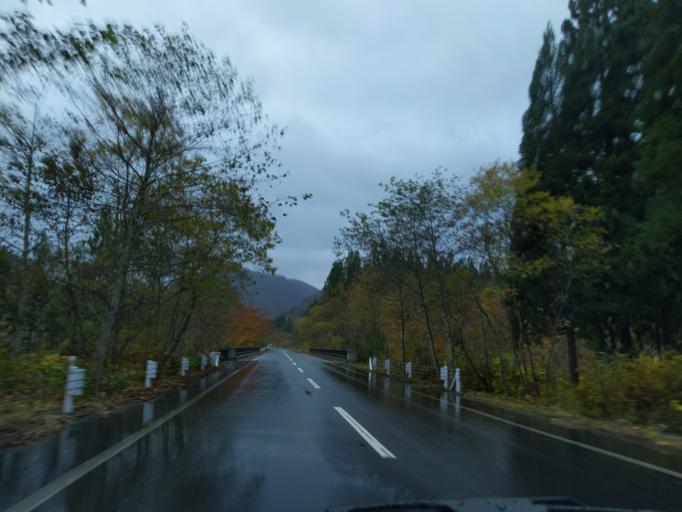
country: JP
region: Iwate
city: Mizusawa
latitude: 39.0762
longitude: 140.8632
